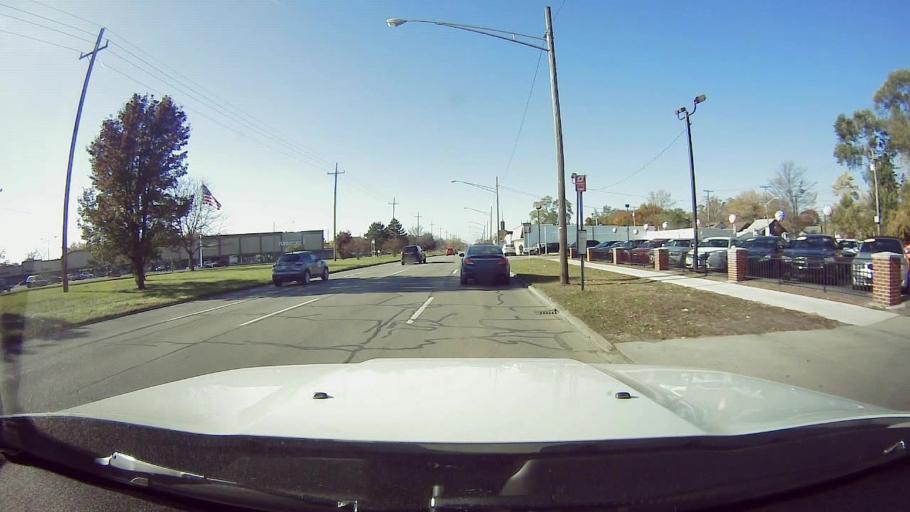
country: US
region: Michigan
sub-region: Wayne County
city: Redford
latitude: 42.4305
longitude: -83.2919
